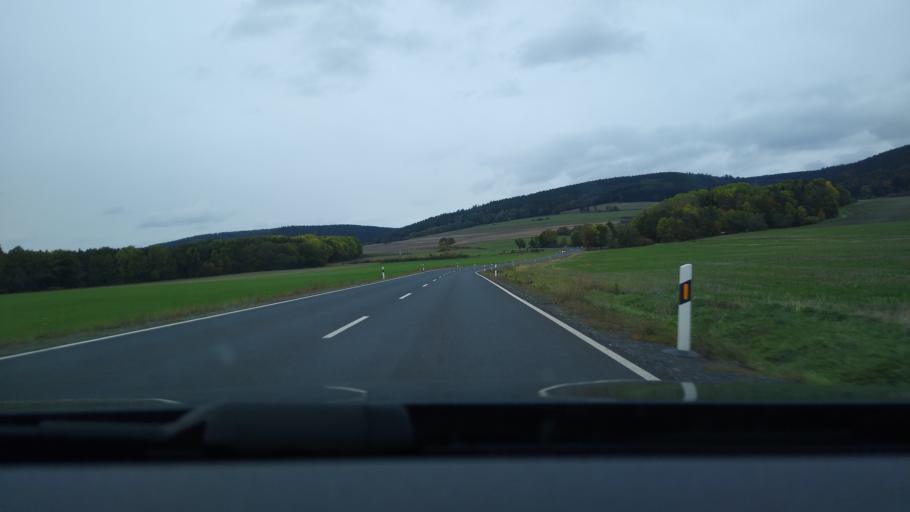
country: DE
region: Thuringia
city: Eisfeld
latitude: 50.4459
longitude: 10.9397
